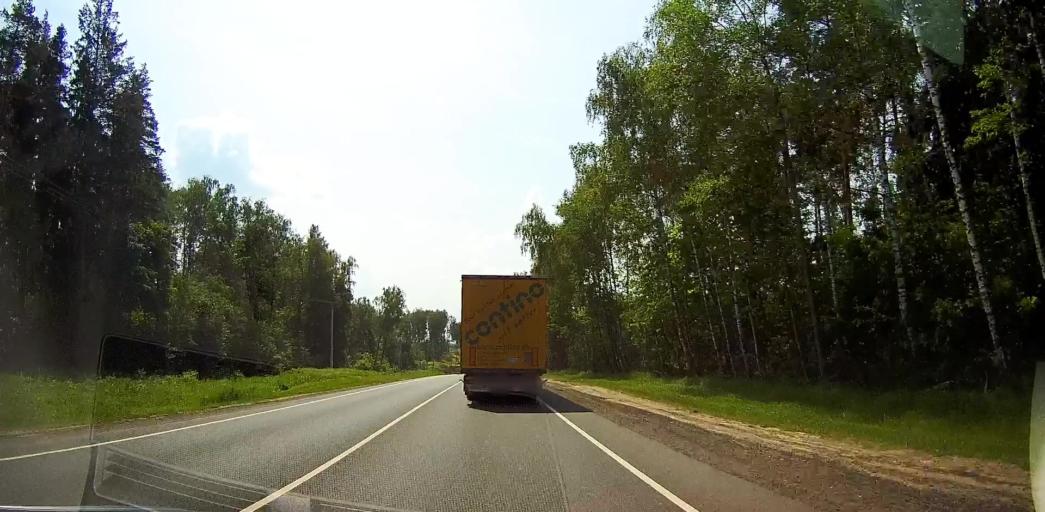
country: RU
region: Moskovskaya
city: Meshcherino
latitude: 55.2040
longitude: 38.3778
